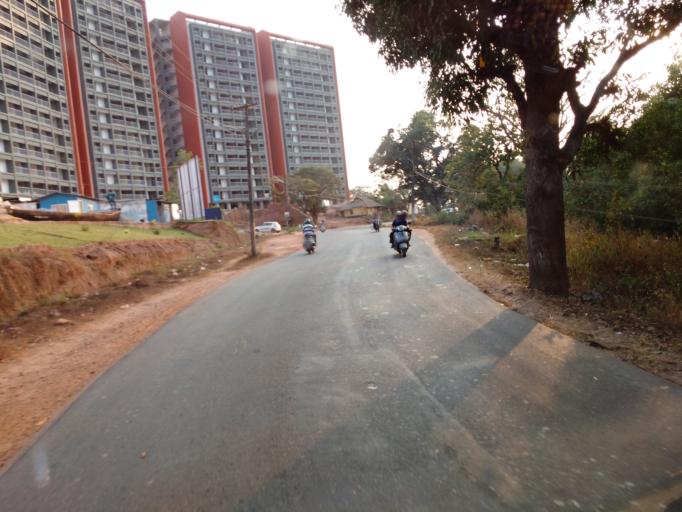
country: IN
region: Karnataka
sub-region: Dakshina Kannada
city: Mangalore
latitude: 12.8935
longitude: 74.8900
